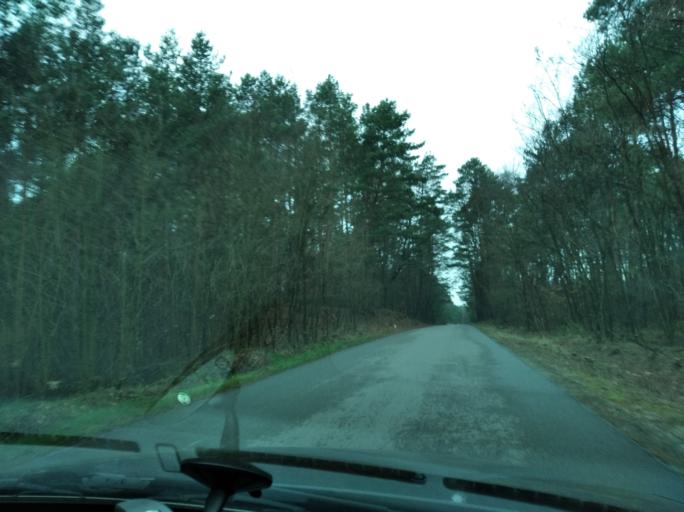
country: PL
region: Subcarpathian Voivodeship
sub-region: Powiat lancucki
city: Brzoza Stadnicka
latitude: 50.2035
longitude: 22.2770
